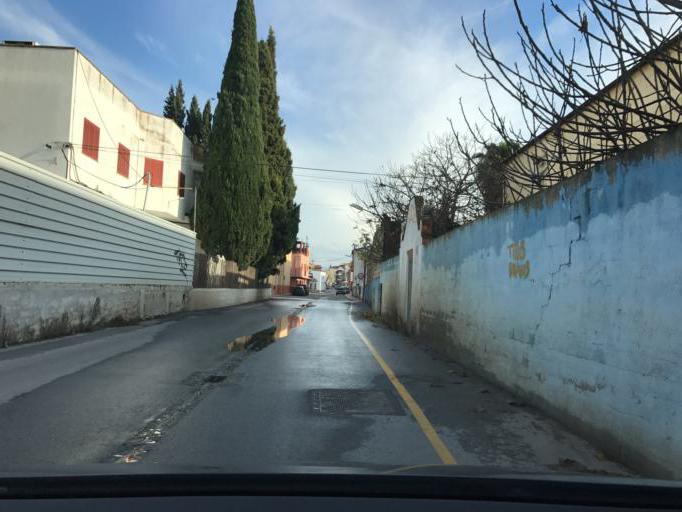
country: ES
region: Andalusia
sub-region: Provincia de Granada
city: Atarfe
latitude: 37.2239
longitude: -3.6965
